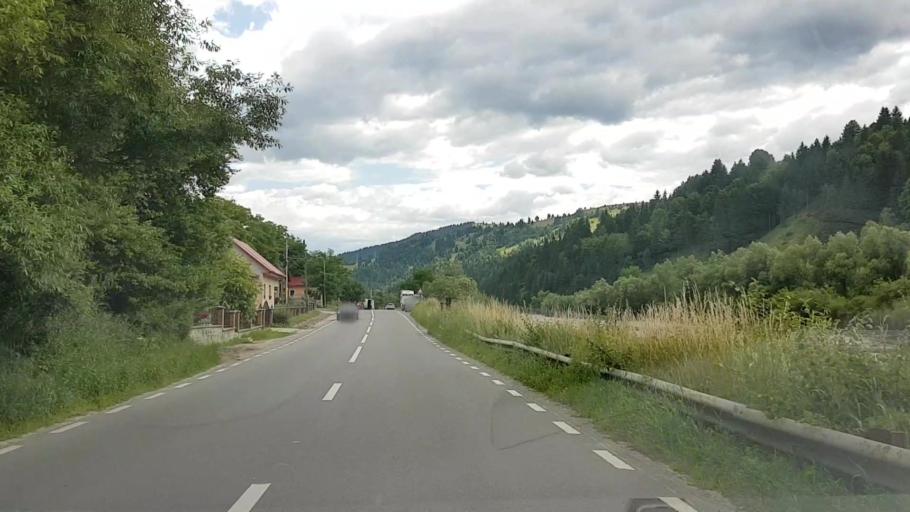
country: RO
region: Neamt
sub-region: Comuna Farcasa
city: Farcasa
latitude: 47.1655
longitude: 25.8084
